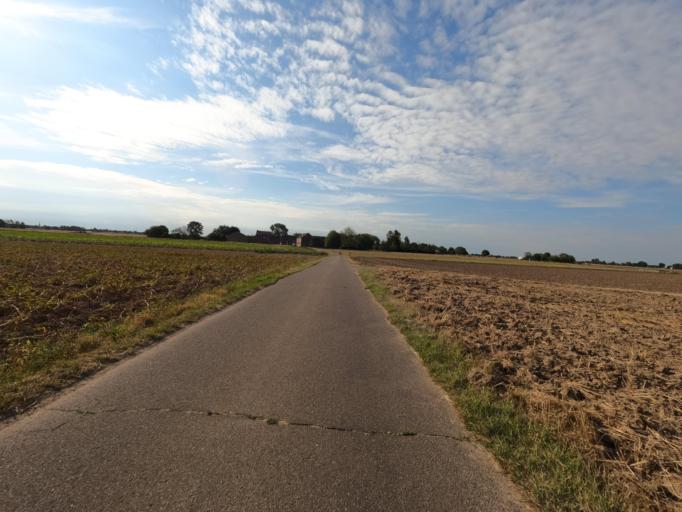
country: DE
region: North Rhine-Westphalia
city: Wegberg
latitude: 51.1088
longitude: 6.2503
